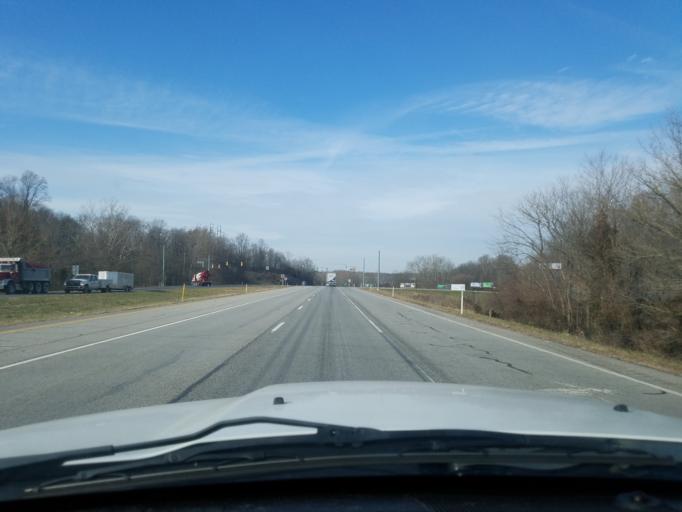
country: US
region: Indiana
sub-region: Monroe County
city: Bloomington
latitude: 39.0843
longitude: -86.5412
